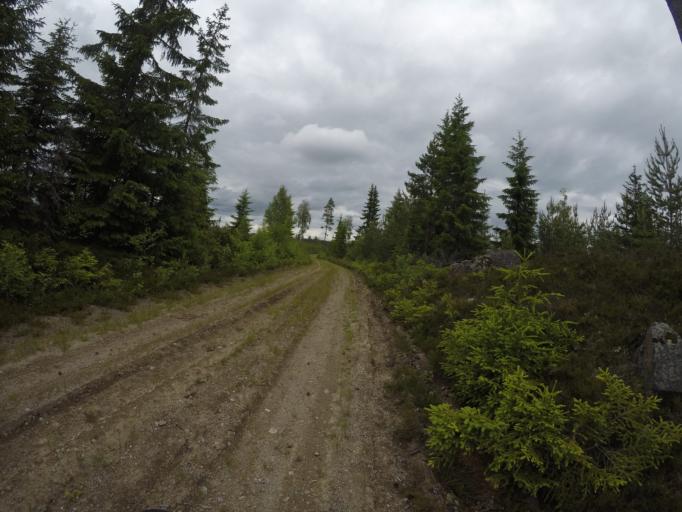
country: SE
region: OErebro
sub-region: Hallefors Kommun
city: Haellefors
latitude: 60.0596
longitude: 14.5263
